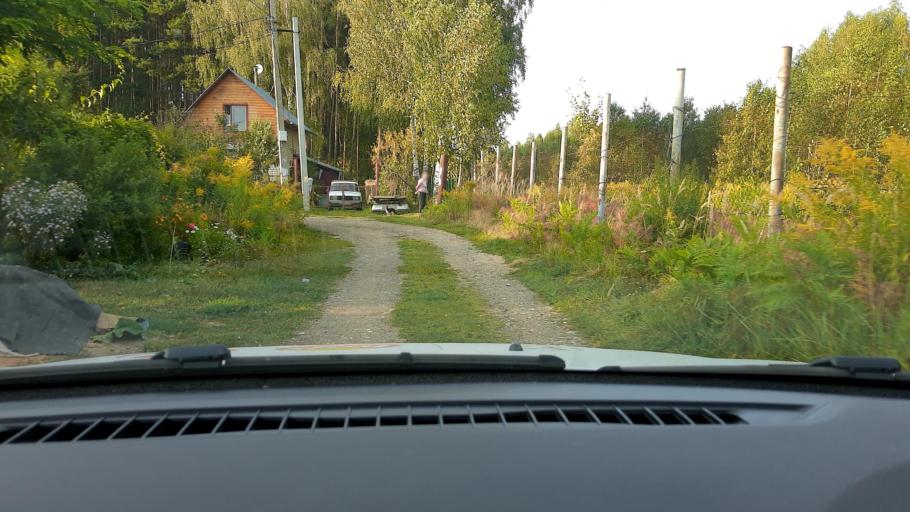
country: RU
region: Nizjnij Novgorod
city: Sitniki
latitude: 56.4217
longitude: 44.0696
